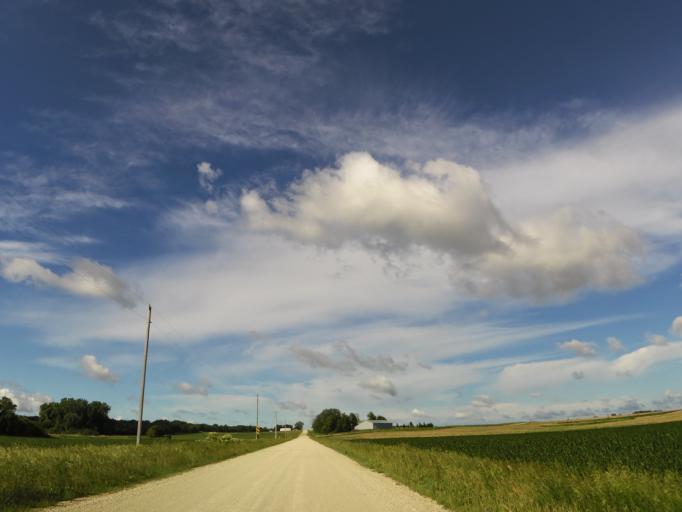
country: US
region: Minnesota
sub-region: Goodhue County
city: Cannon Falls
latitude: 44.6250
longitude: -92.9629
